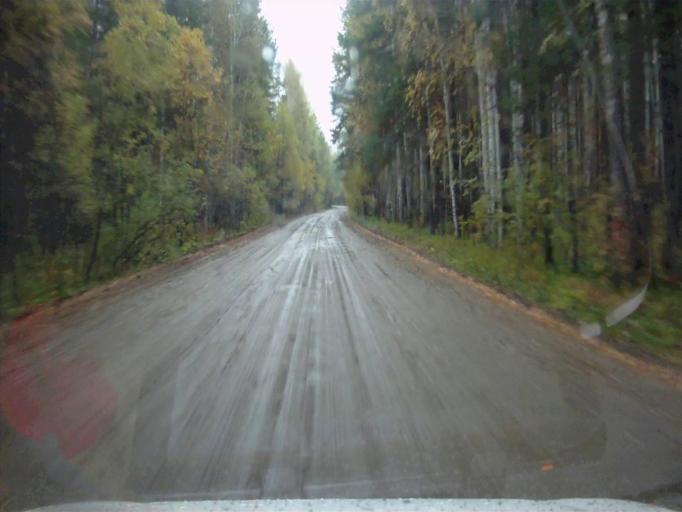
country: RU
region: Chelyabinsk
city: Kyshtym
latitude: 55.8892
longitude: 60.4650
